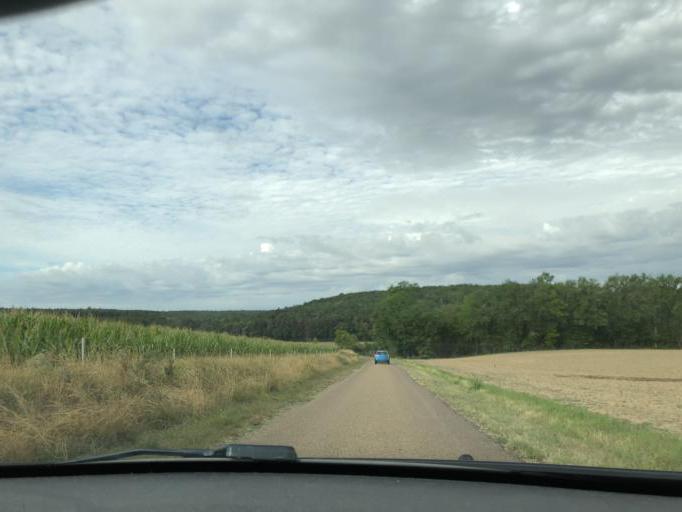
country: FR
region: Bourgogne
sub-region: Departement de l'Yonne
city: Chablis
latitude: 47.7768
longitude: 3.8148
